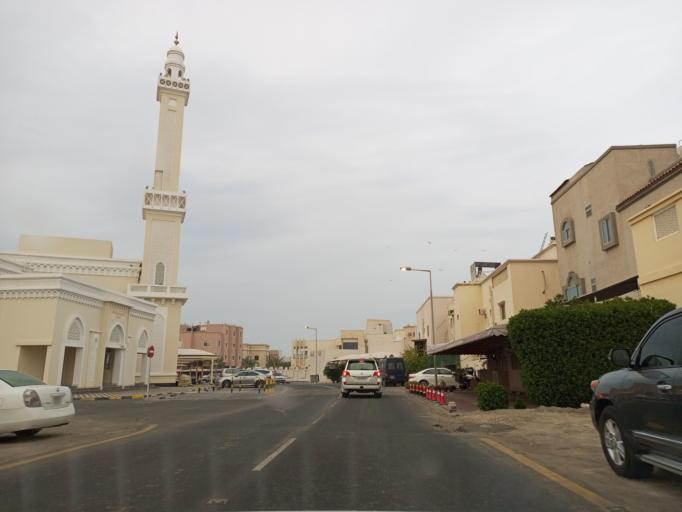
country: BH
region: Muharraq
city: Al Hadd
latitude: 26.2440
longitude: 50.6480
